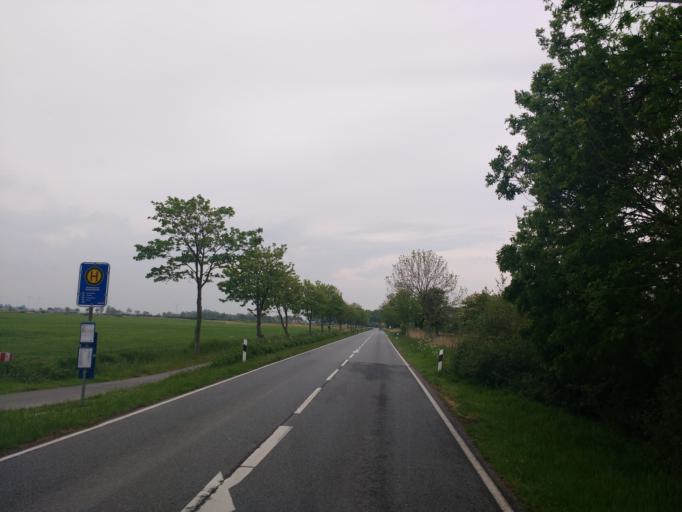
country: DE
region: Lower Saxony
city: Neuharlingersiel
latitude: 53.6943
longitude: 7.6897
